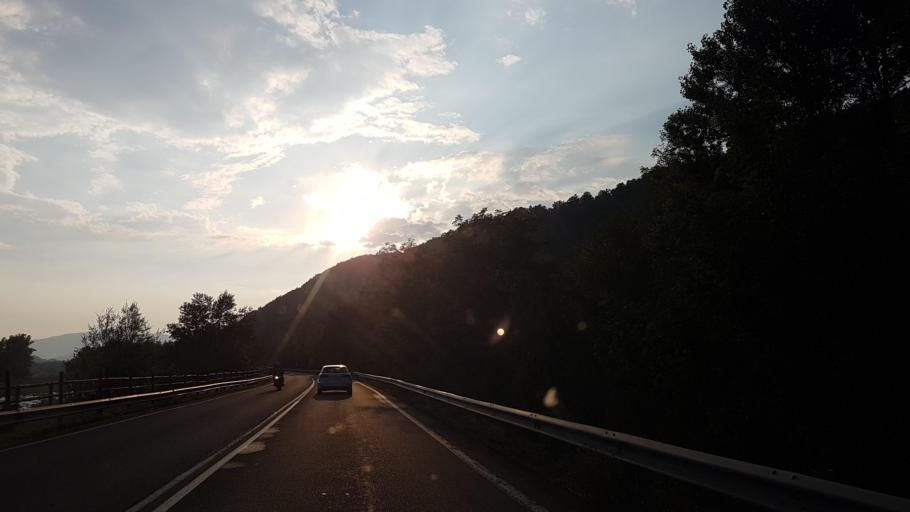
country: IT
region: Emilia-Romagna
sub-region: Provincia di Parma
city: Borgo Val di Taro
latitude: 44.5010
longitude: 9.8115
